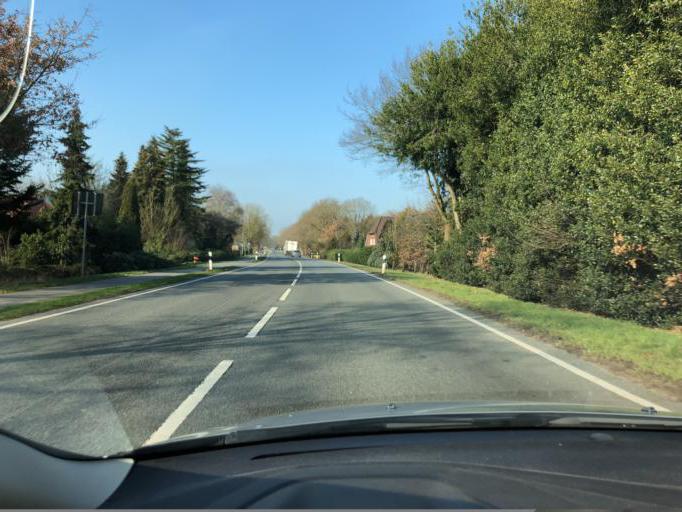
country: DE
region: Lower Saxony
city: Westerstede
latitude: 53.2913
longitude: 7.8843
